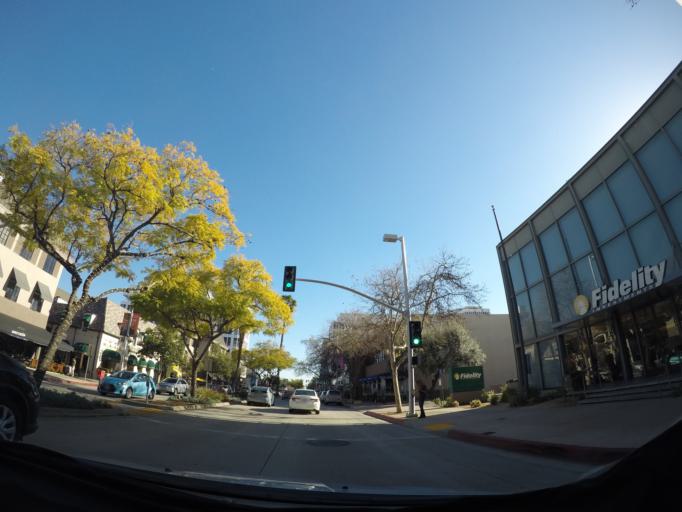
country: US
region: California
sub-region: Los Angeles County
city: Pasadena
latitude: 34.1438
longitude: -118.1325
